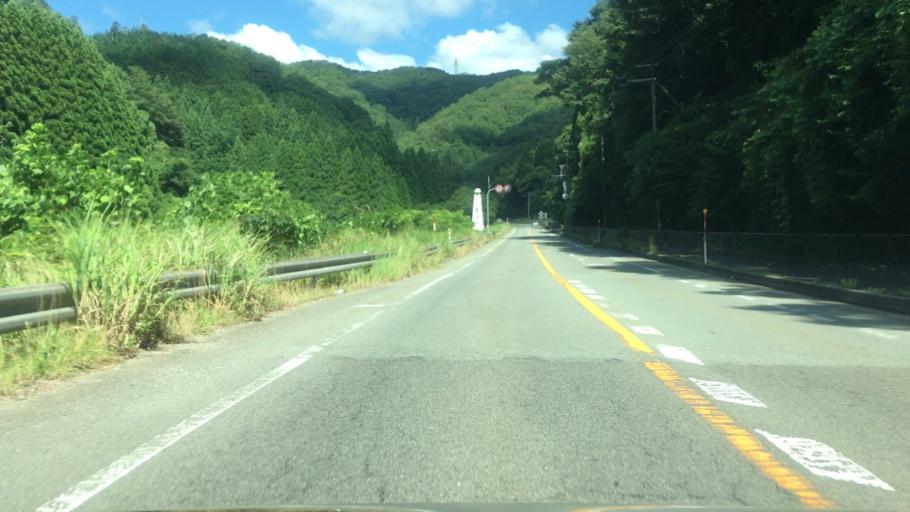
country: JP
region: Hyogo
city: Toyooka
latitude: 35.5762
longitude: 134.7554
